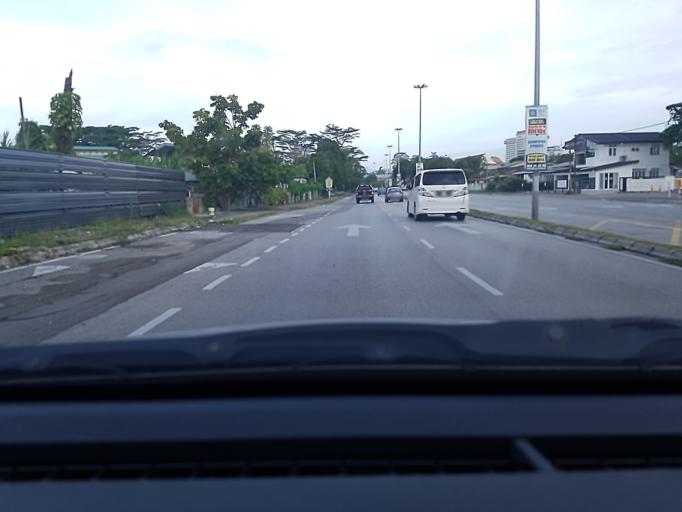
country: MY
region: Sarawak
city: Kuching
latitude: 1.5279
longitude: 110.3666
